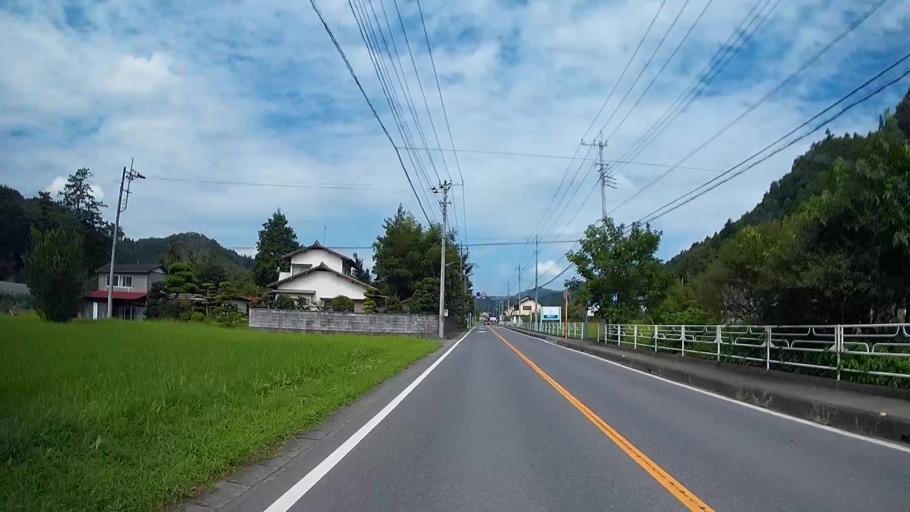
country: JP
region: Saitama
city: Hanno
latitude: 35.8624
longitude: 139.2909
